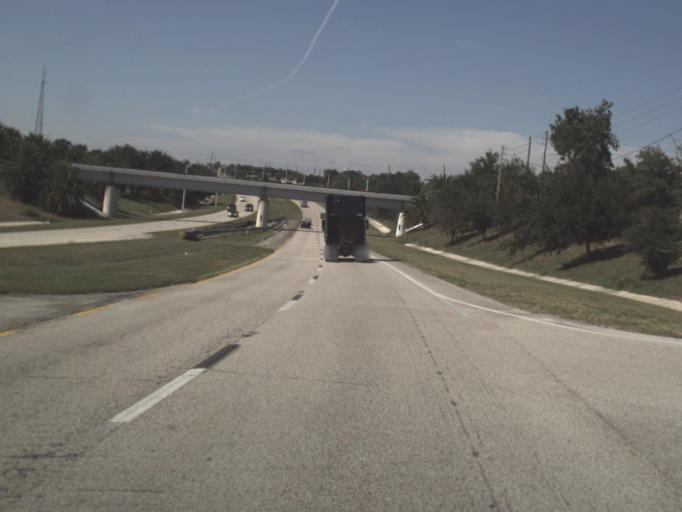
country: US
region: Florida
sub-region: Highlands County
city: Lake Placid
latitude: 27.3139
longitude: -81.3596
